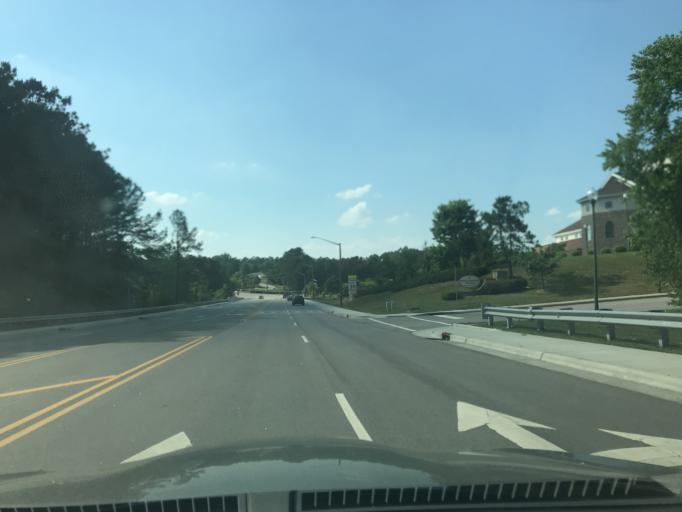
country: US
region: North Carolina
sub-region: Wake County
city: Wake Forest
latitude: 35.9479
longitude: -78.5071
